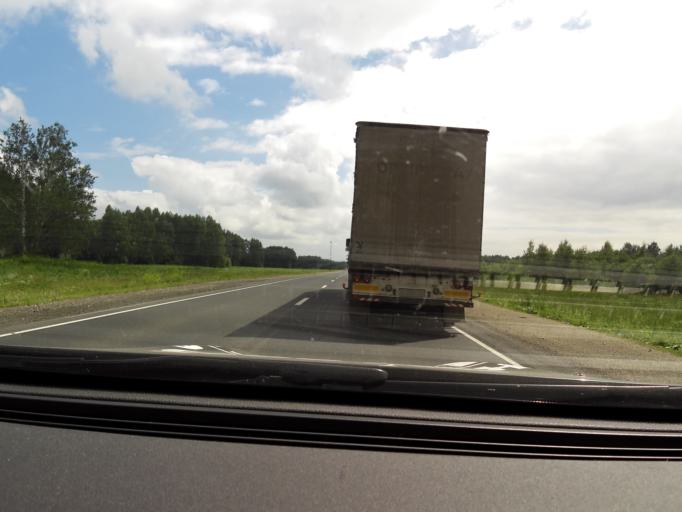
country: RU
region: Perm
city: Orda
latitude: 57.2043
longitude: 57.1027
